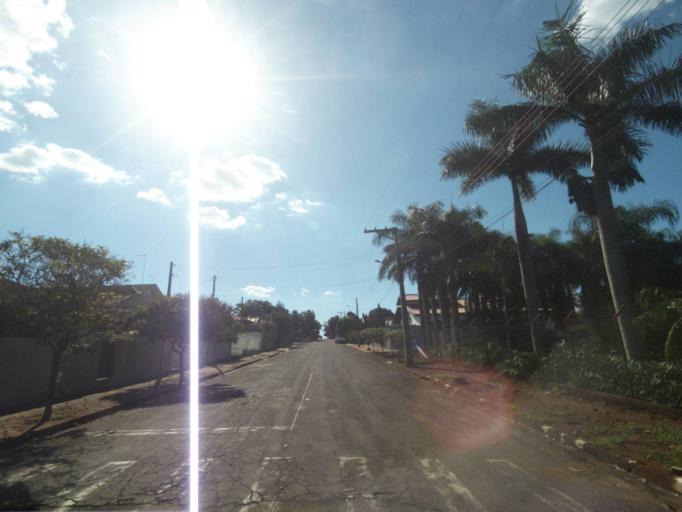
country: BR
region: Parana
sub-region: Sertanopolis
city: Sertanopolis
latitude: -23.0349
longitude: -50.8167
